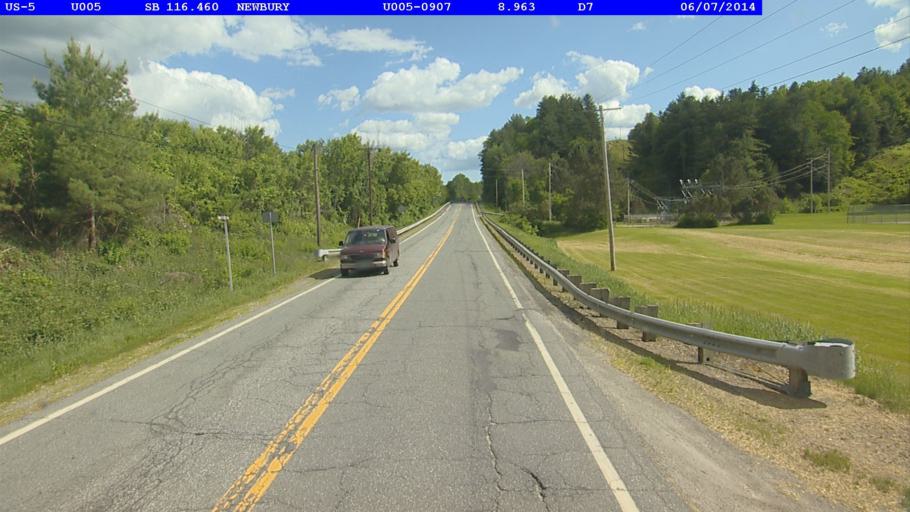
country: US
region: New Hampshire
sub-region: Grafton County
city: Woodsville
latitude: 44.1471
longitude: -72.0433
